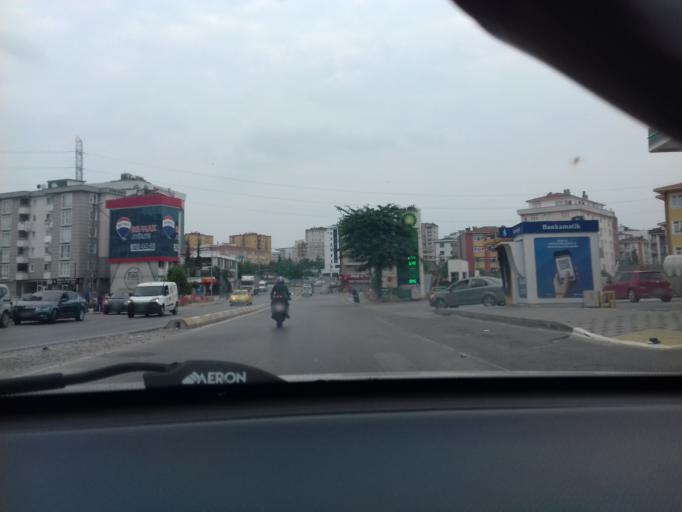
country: TR
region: Istanbul
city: Pendik
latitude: 40.9149
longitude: 29.3034
